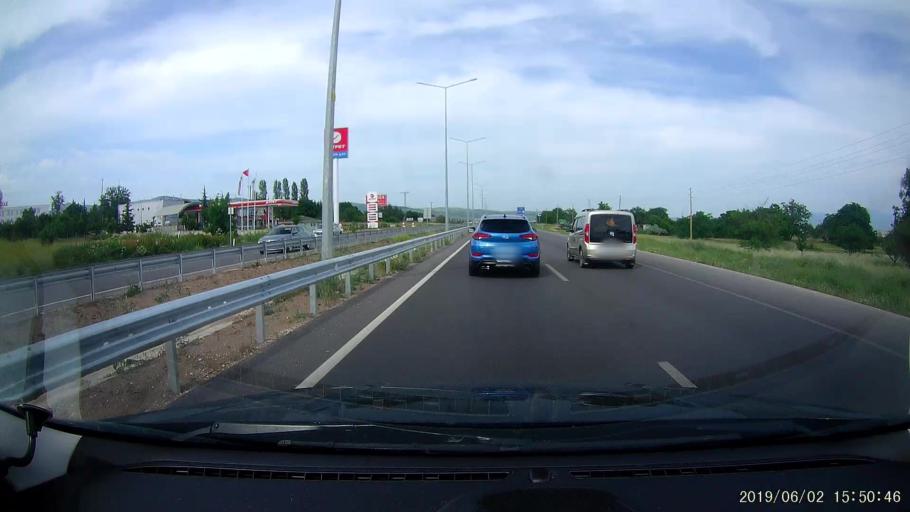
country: TR
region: Amasya
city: Merzifon
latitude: 40.8621
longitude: 35.4851
